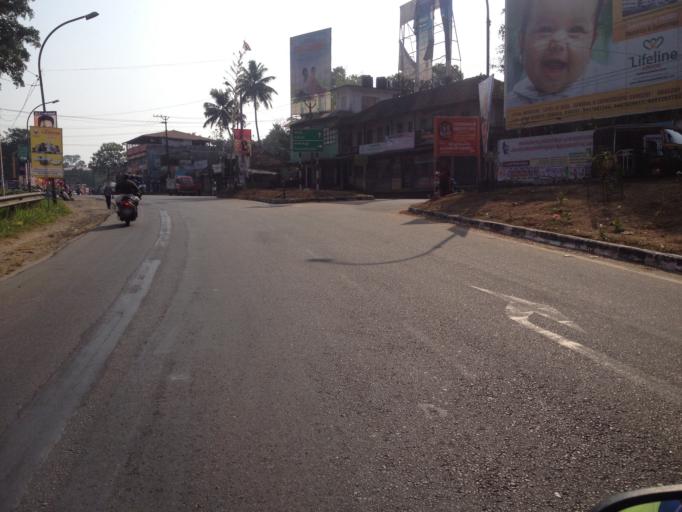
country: IN
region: Kerala
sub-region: Pattanamtitta
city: Adur
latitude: 9.1615
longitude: 76.7202
